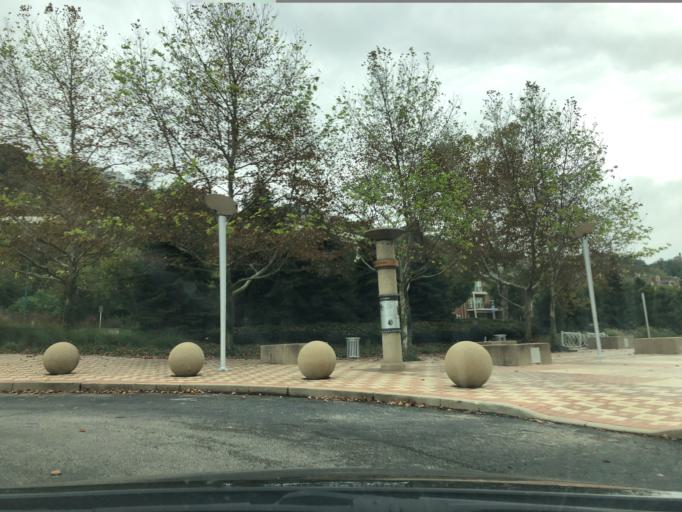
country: US
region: Kentucky
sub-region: Campbell County
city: Bellevue
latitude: 39.1062
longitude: -84.4928
